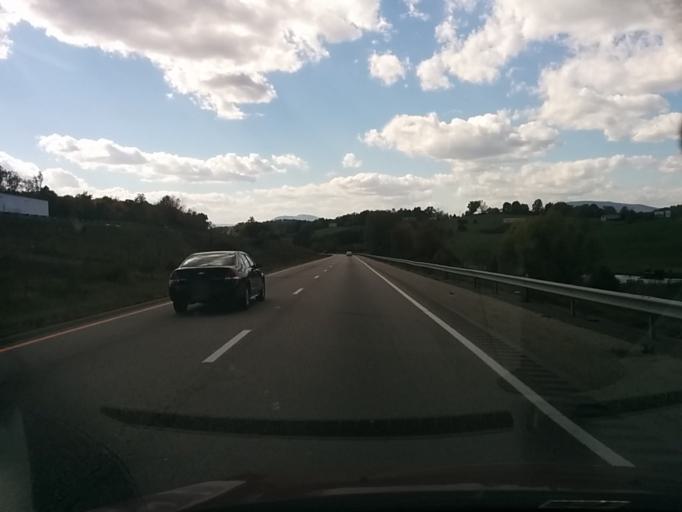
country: US
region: Virginia
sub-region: Rockbridge County
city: East Lexington
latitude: 37.8703
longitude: -79.3235
